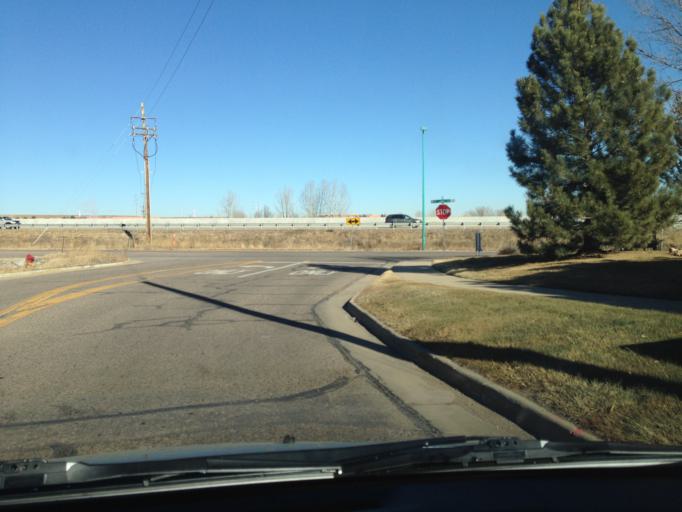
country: US
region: Colorado
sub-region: Boulder County
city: Superior
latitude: 39.9605
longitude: -105.1752
